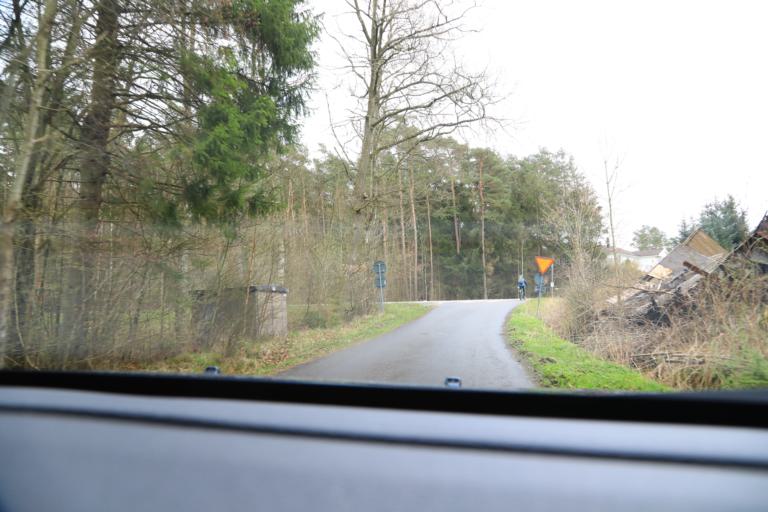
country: SE
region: Halland
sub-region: Kungsbacka Kommun
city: Frillesas
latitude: 57.3082
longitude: 12.1810
